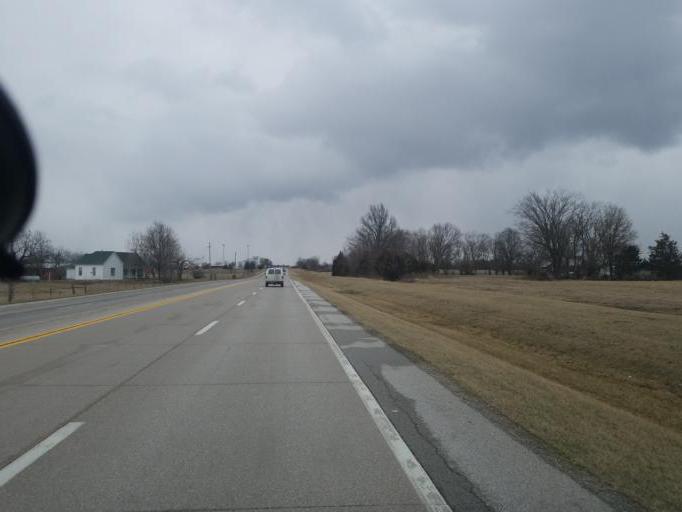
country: US
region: Missouri
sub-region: Macon County
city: Macon
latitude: 39.7757
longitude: -92.4764
